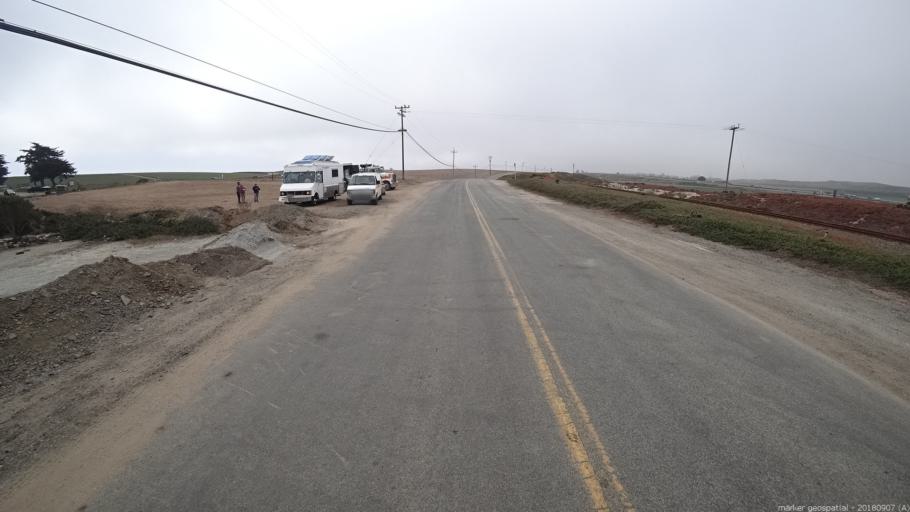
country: US
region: California
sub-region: Monterey County
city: Marina
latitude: 36.7215
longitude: -121.7885
